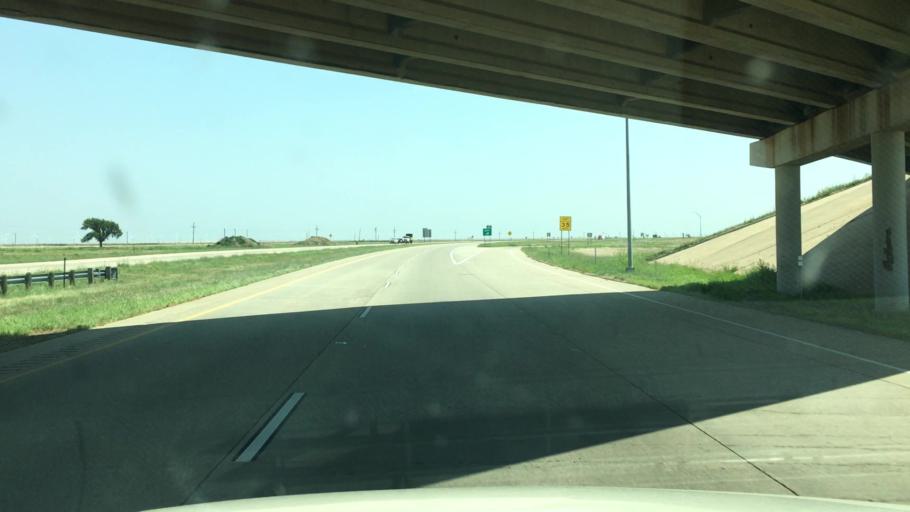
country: US
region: Texas
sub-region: Oldham County
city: Vega
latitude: 35.2386
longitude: -102.4059
